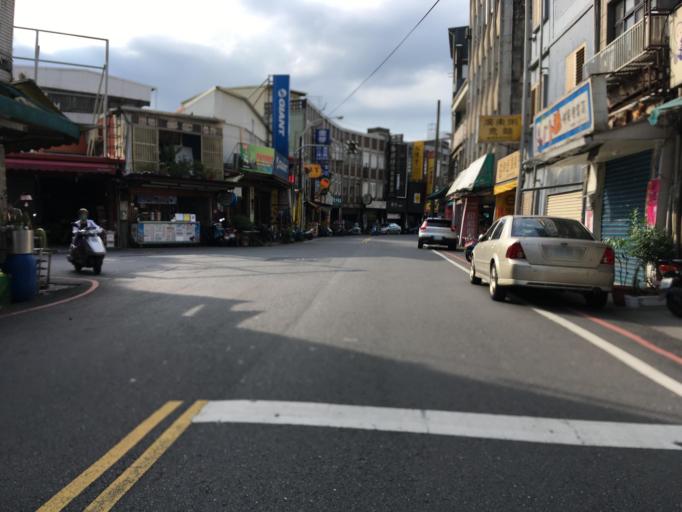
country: TW
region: Taiwan
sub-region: Yilan
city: Yilan
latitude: 24.6718
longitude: 121.7704
